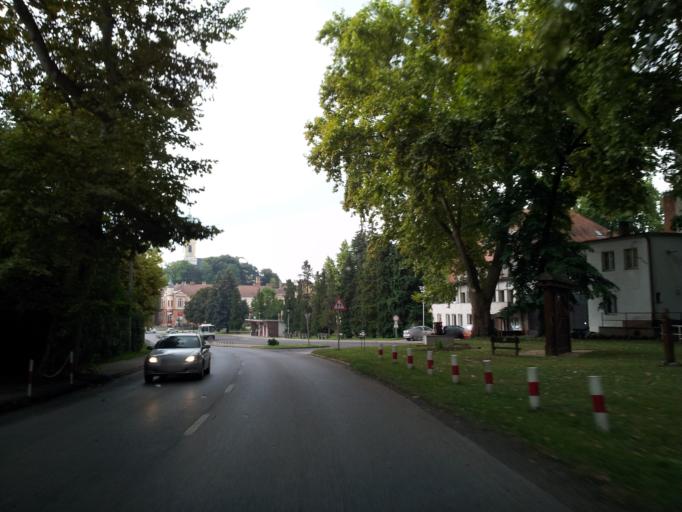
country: HU
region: Tolna
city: Hogyesz
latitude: 46.4975
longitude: 18.4166
